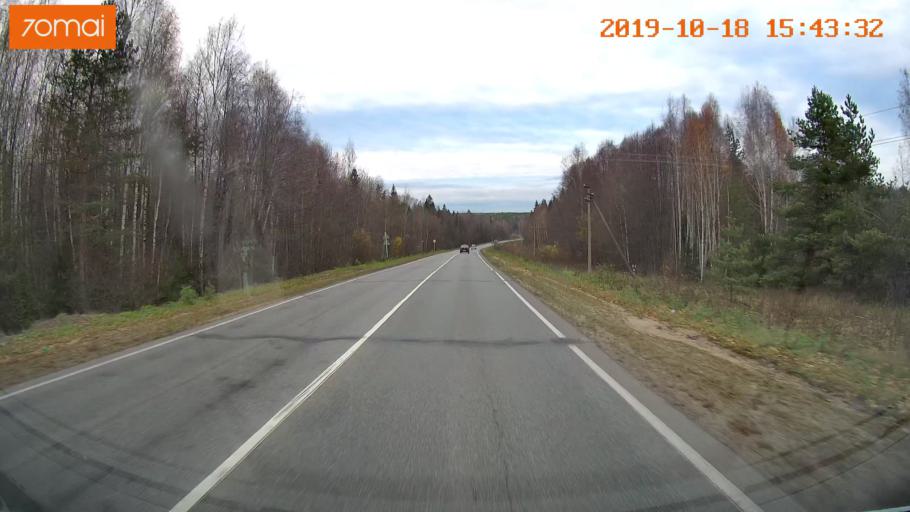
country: RU
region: Vladimir
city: Golovino
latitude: 55.9689
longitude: 40.5499
